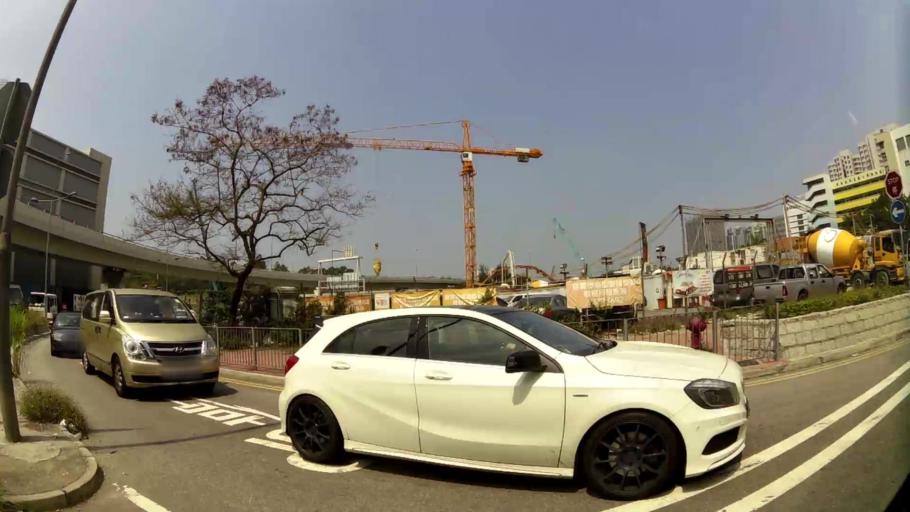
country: HK
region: Sham Shui Po
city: Sham Shui Po
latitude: 22.3125
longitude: 114.1645
